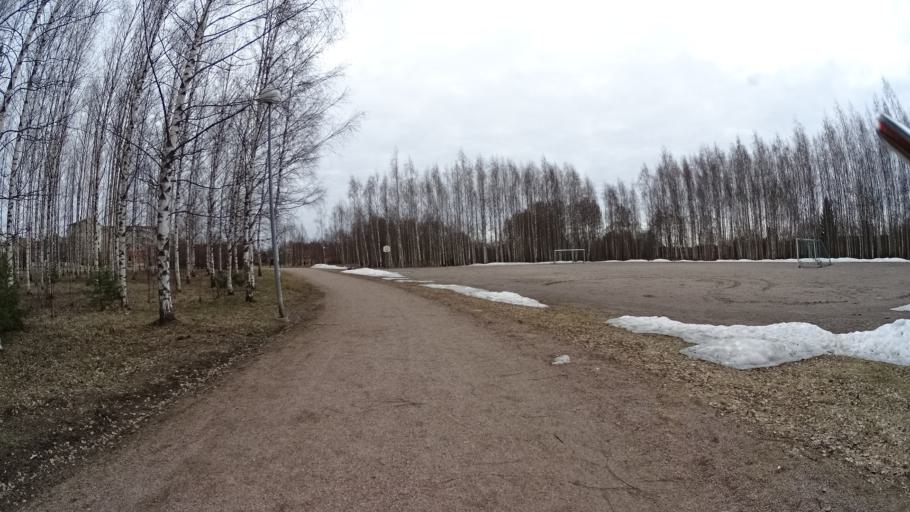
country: FI
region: Uusimaa
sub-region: Helsinki
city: Vantaa
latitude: 60.2872
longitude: 24.9406
